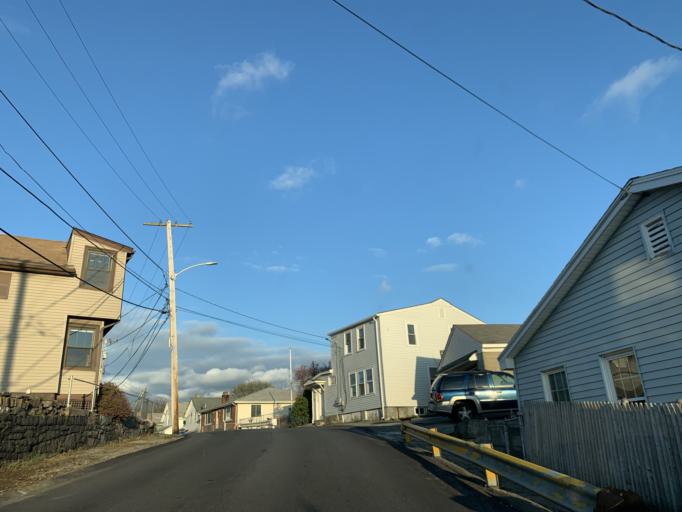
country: US
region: Rhode Island
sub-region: Providence County
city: Valley Falls
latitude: 41.8998
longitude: -71.3834
